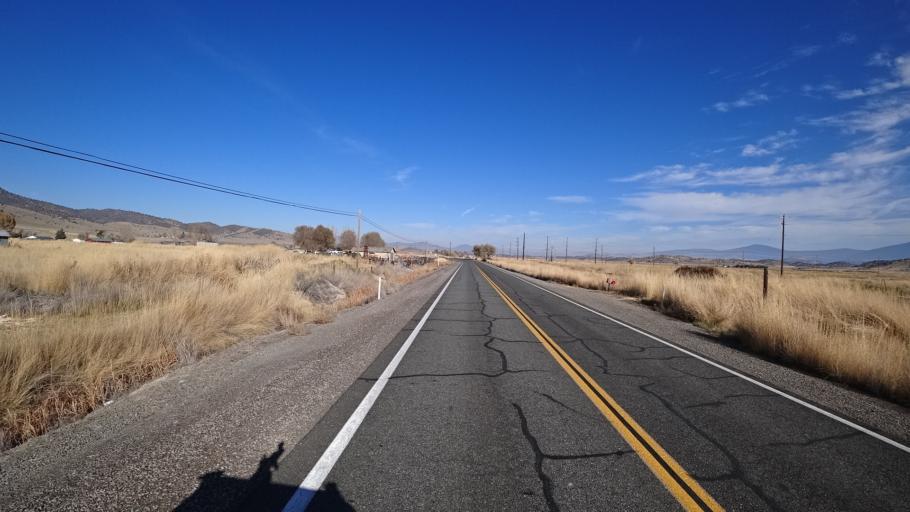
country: US
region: California
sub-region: Siskiyou County
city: Montague
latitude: 41.6013
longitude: -122.5235
